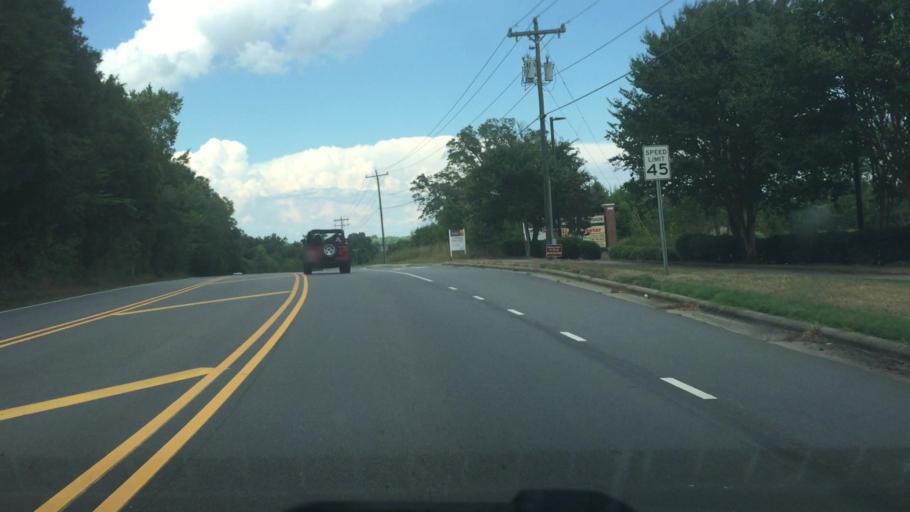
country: US
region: North Carolina
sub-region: Mecklenburg County
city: Huntersville
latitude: 35.4196
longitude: -80.7444
